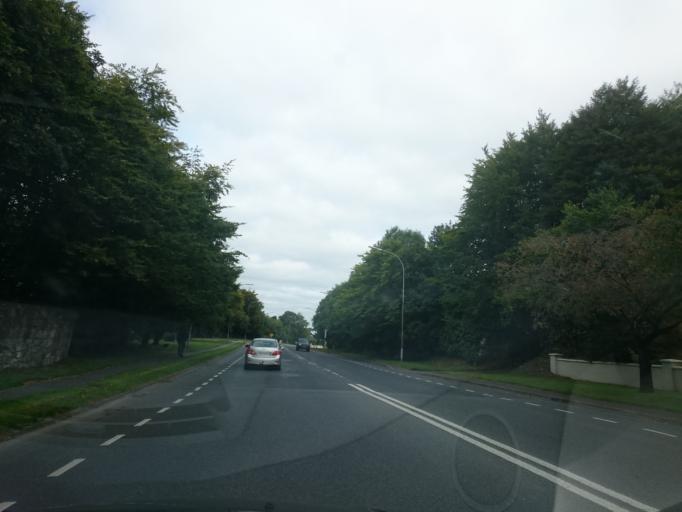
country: IE
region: Leinster
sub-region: Kilkenny
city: Kilkenny
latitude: 52.6705
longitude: -7.2529
